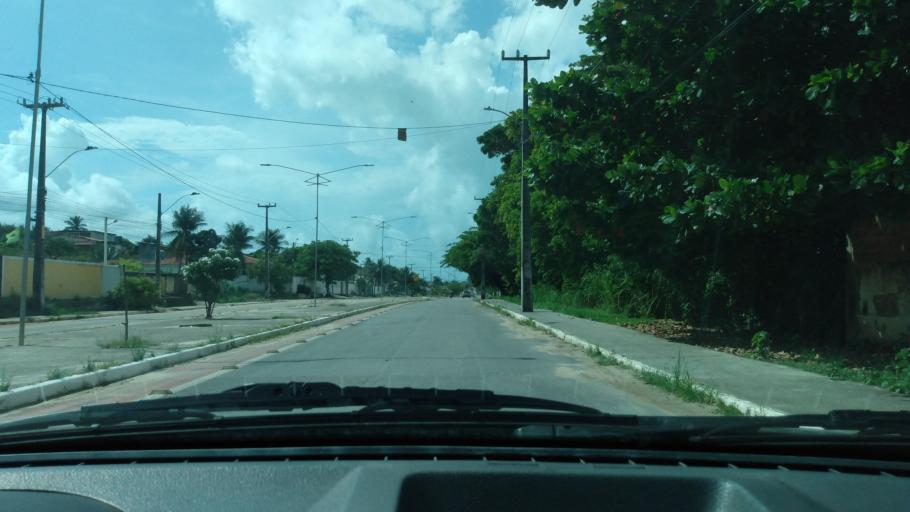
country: BR
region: Pernambuco
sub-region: Cabo De Santo Agostinho
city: Cabo
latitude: -8.3178
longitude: -34.9509
